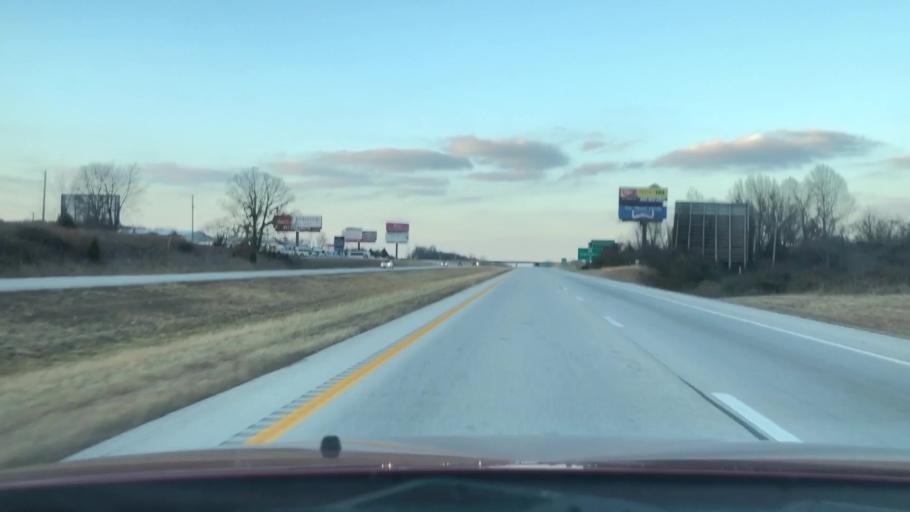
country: US
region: Missouri
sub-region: Christian County
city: Ozark
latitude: 36.9361
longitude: -93.2321
